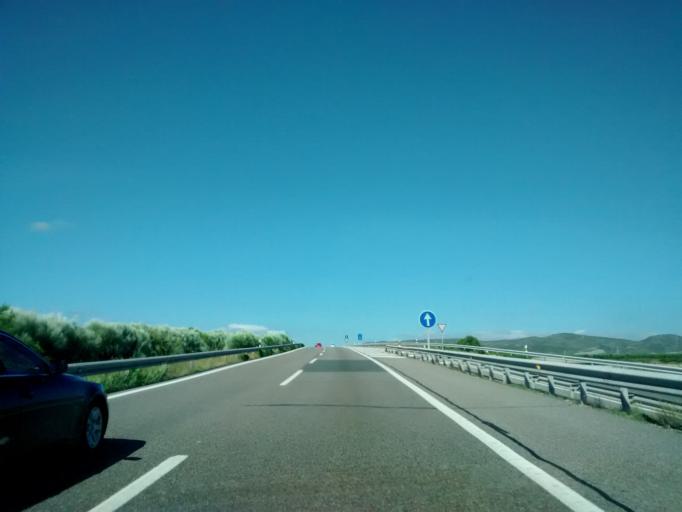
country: ES
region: Aragon
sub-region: Provincia de Zaragoza
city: La Almunia de Dona Godina
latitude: 41.4847
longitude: -1.3835
